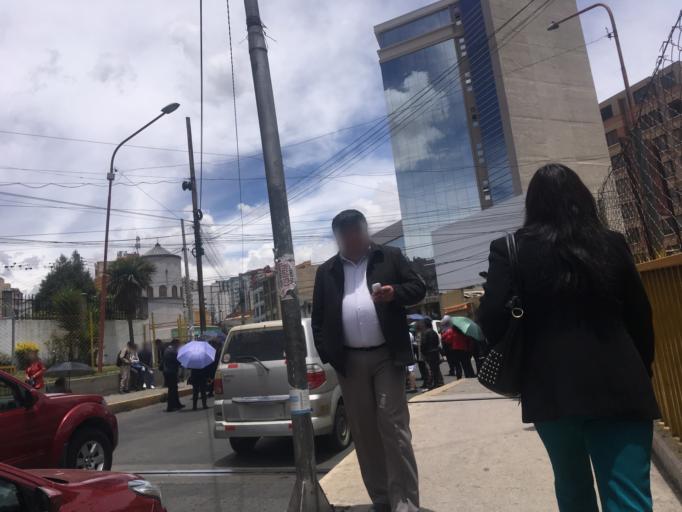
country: BO
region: La Paz
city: La Paz
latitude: -16.5069
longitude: -68.1222
